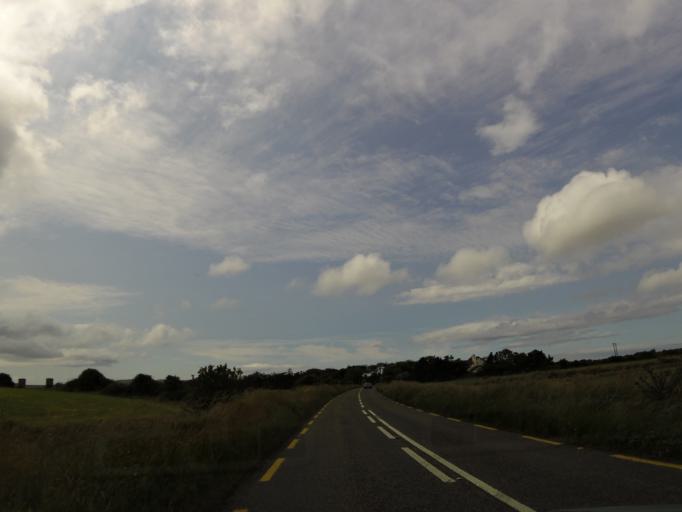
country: IE
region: Munster
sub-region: An Clar
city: Kilrush
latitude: 52.6737
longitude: -9.6012
